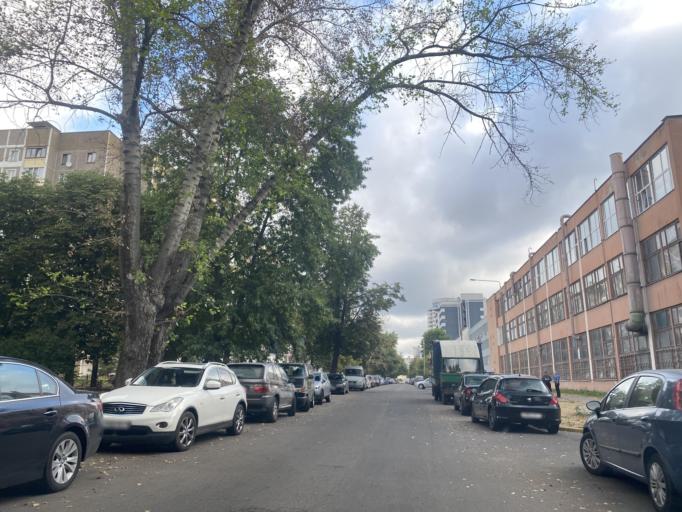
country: BY
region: Minsk
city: Minsk
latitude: 53.9193
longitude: 27.5619
